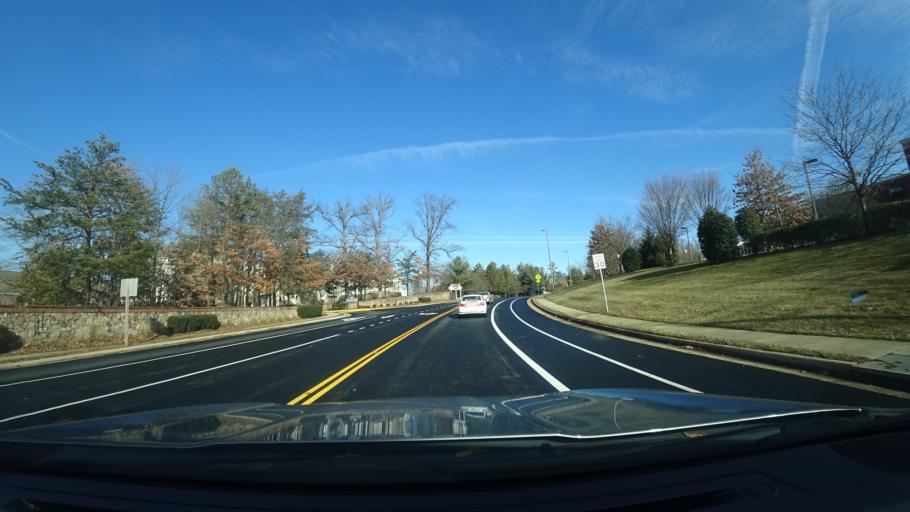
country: US
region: Virginia
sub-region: Fairfax County
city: Reston
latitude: 38.9665
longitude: -77.3602
